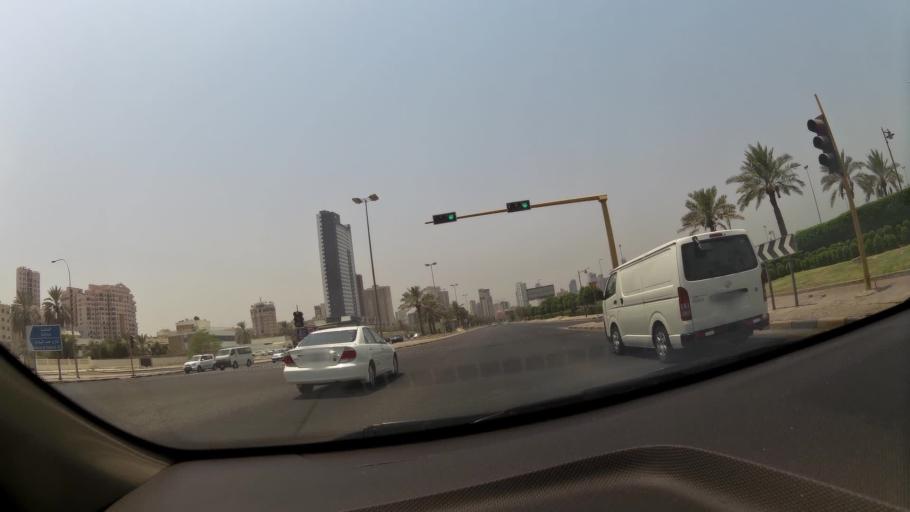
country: KW
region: Muhafazat Hawalli
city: As Salimiyah
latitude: 29.3377
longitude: 48.0723
